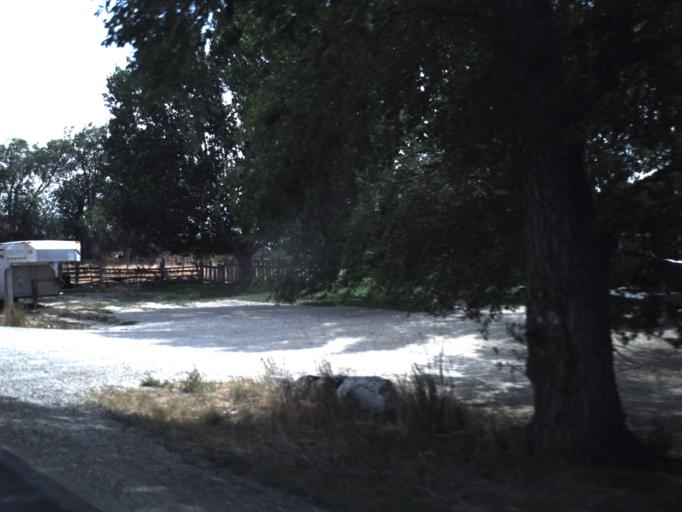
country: US
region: Idaho
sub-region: Cassia County
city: Burley
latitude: 41.8170
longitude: -113.3231
